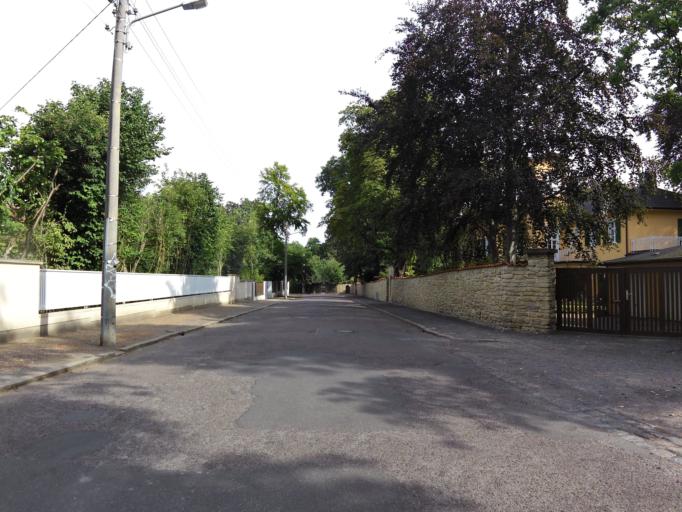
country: DE
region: Saxony
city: Leipzig
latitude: 51.3591
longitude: 12.2975
